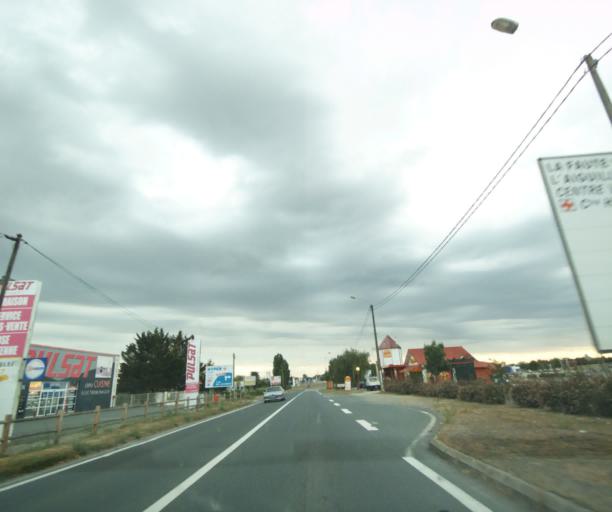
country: FR
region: Pays de la Loire
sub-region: Departement de la Vendee
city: Lucon
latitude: 46.4591
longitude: -1.1439
